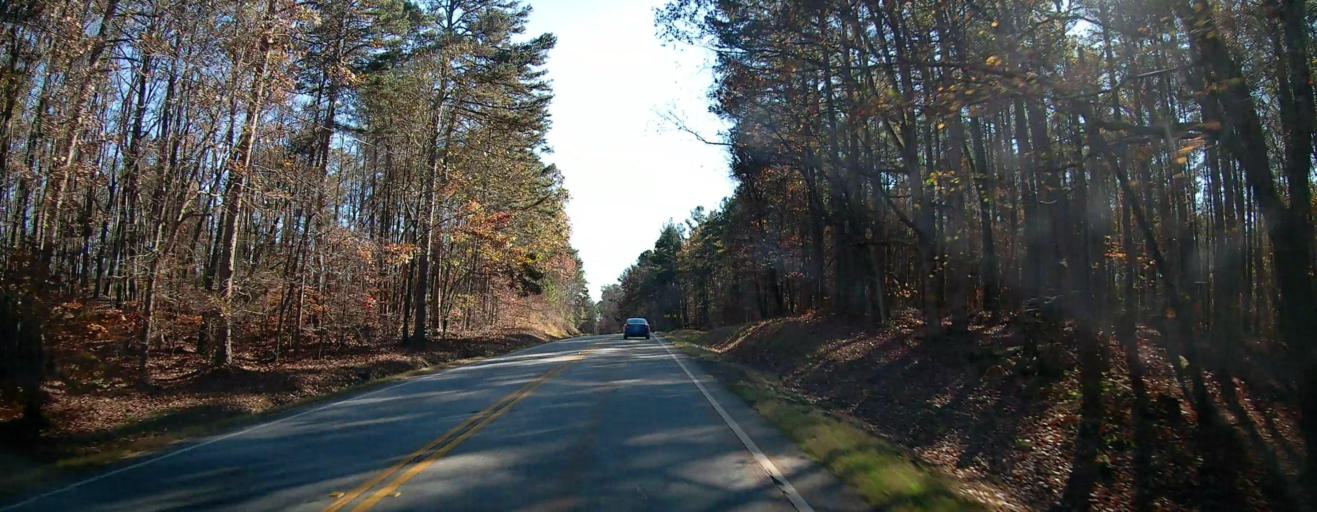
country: US
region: Georgia
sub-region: Hall County
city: Lula
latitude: 34.4354
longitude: -83.7179
